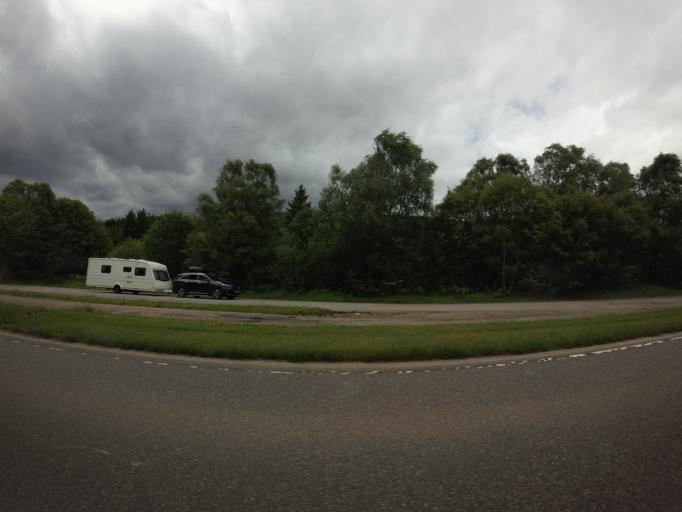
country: GB
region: Scotland
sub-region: Highland
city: Dingwall
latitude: 57.6808
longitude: -4.6713
